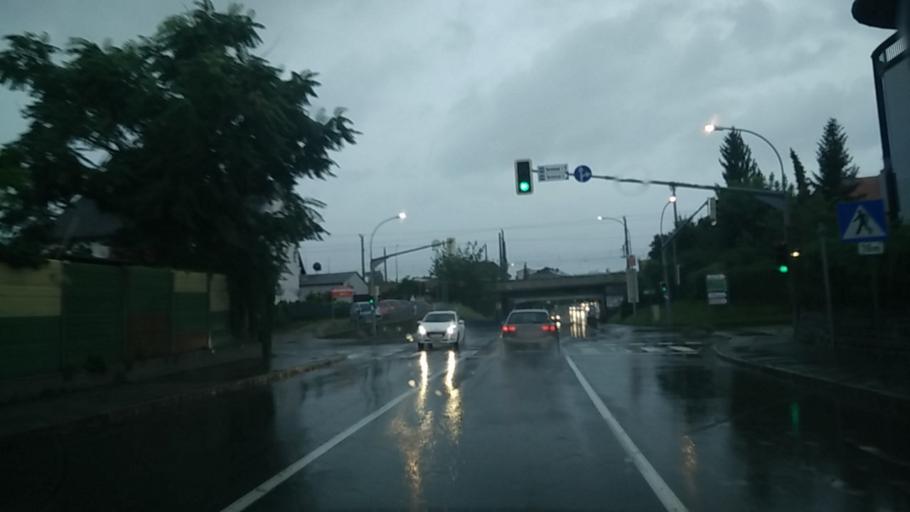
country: AT
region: Carinthia
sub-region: Villach Stadt
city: Villach
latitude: 46.6214
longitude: 13.8607
